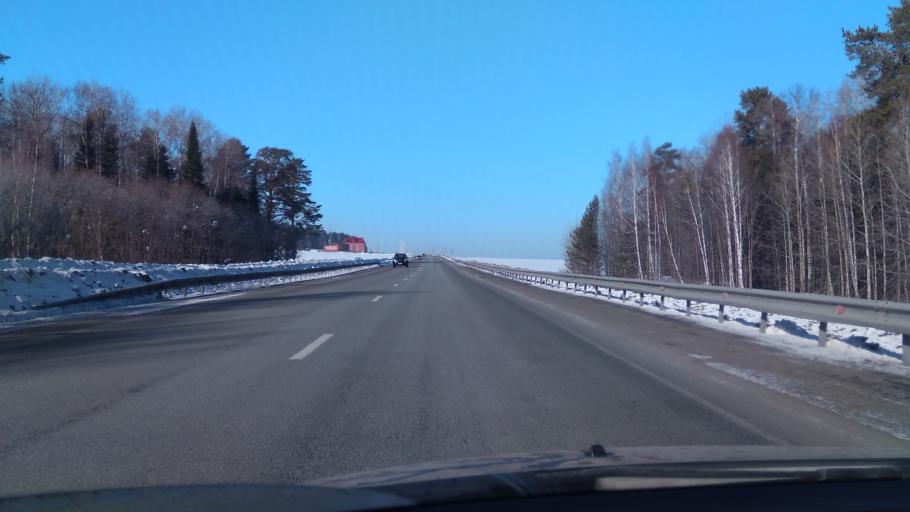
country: RU
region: Sverdlovsk
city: Bisert'
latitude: 56.8323
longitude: 58.8112
